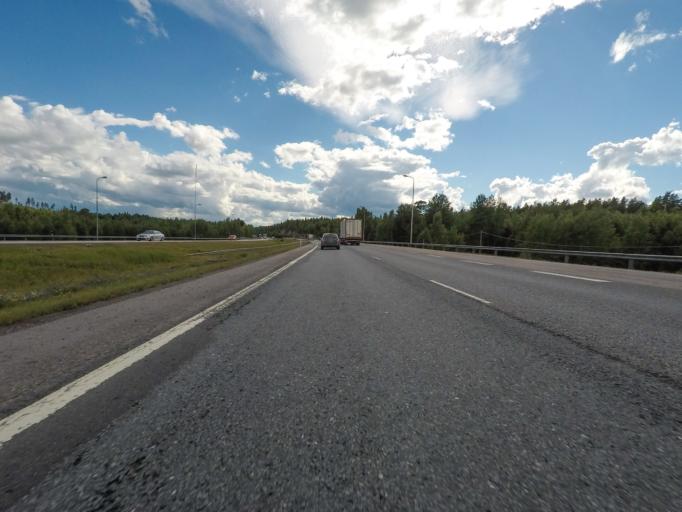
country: FI
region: Paijanne Tavastia
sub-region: Lahti
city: Hollola
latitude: 60.8246
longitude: 25.5223
